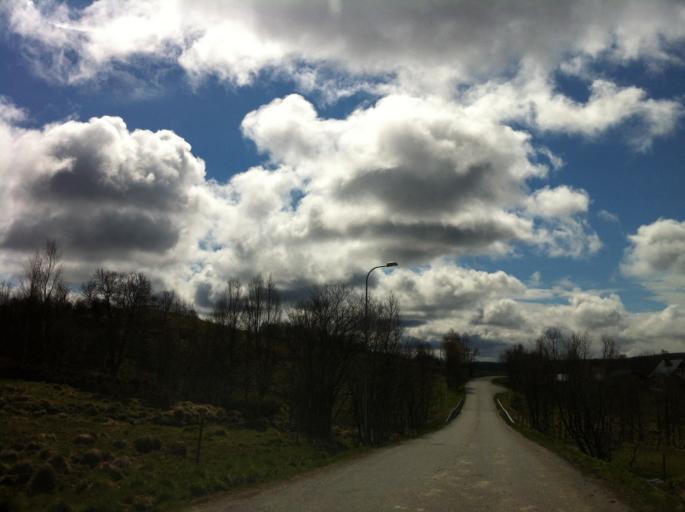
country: NO
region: Sor-Trondelag
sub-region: Tydal
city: Aas
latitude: 62.6427
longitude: 12.4426
